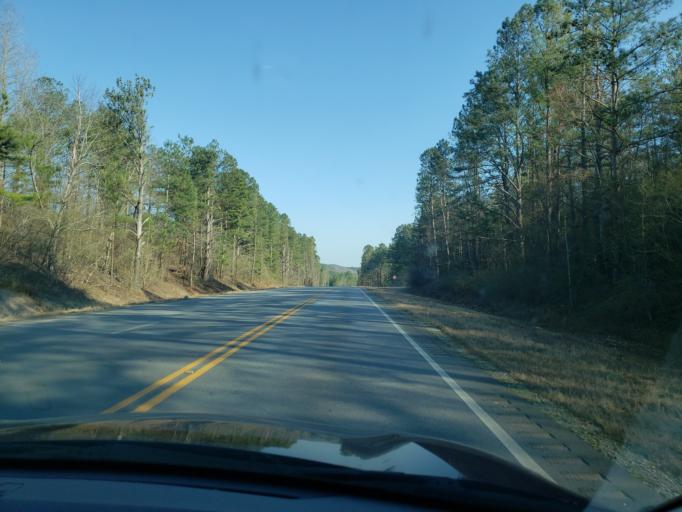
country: US
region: Alabama
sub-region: Randolph County
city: Wedowee
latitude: 33.4081
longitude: -85.5376
